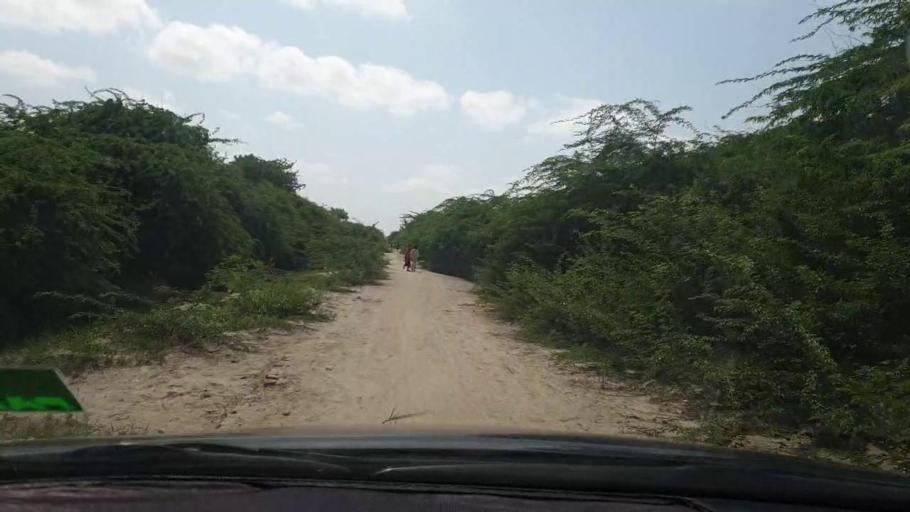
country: PK
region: Sindh
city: Tando Bago
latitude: 24.8684
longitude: 69.0712
